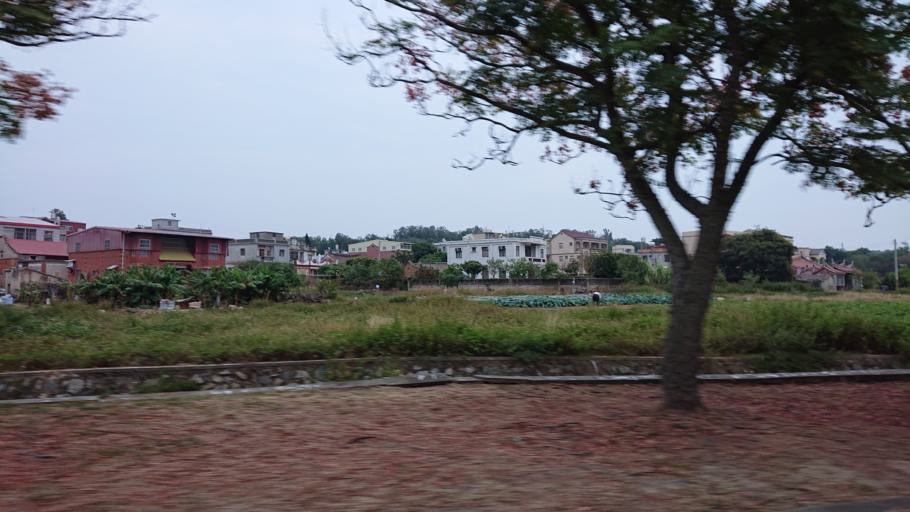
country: TW
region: Fukien
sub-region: Kinmen
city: Jincheng
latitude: 24.4271
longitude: 118.2289
